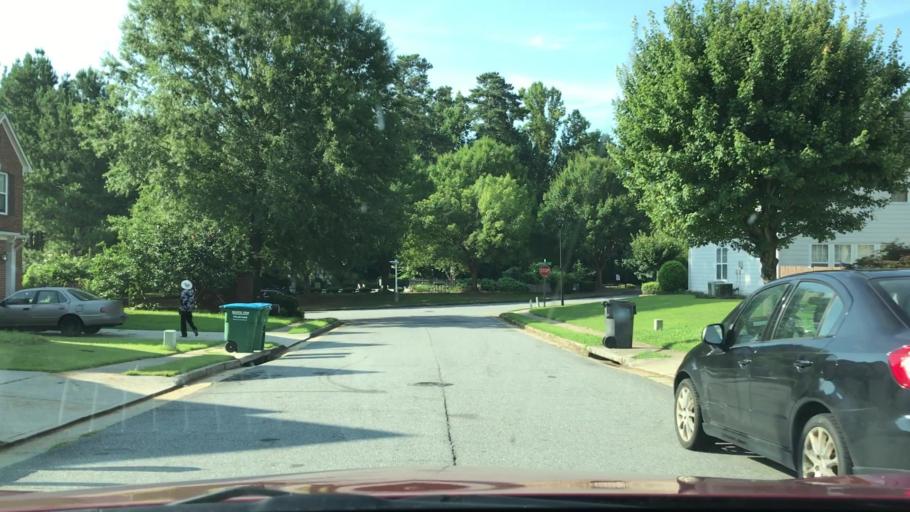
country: US
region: Georgia
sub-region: DeKalb County
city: Tucker
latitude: 33.8814
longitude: -84.1904
